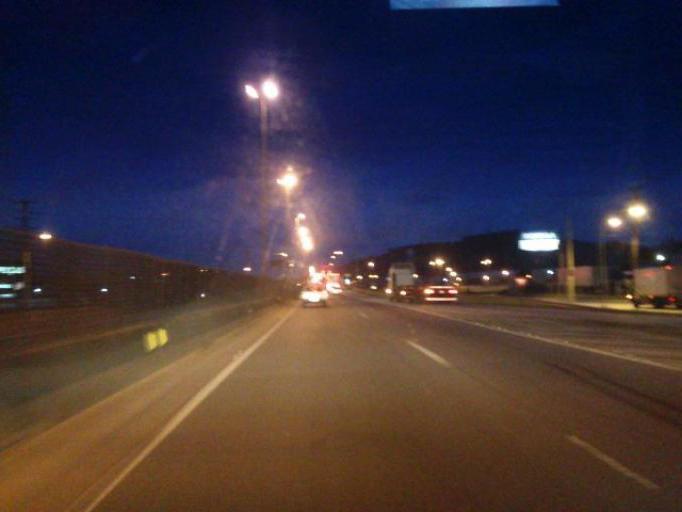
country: BR
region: Santa Catarina
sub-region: Itajai
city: Itajai
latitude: -26.8876
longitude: -48.7224
